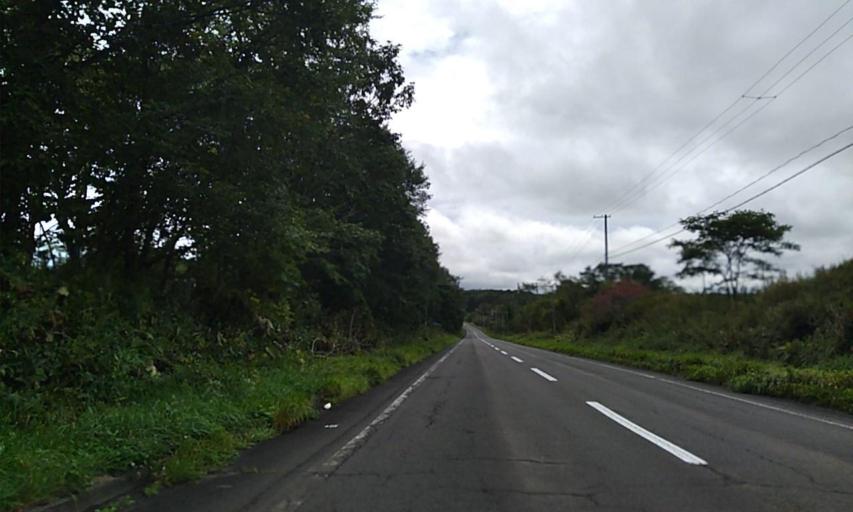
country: JP
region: Hokkaido
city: Shibetsu
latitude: 43.3232
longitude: 145.2151
